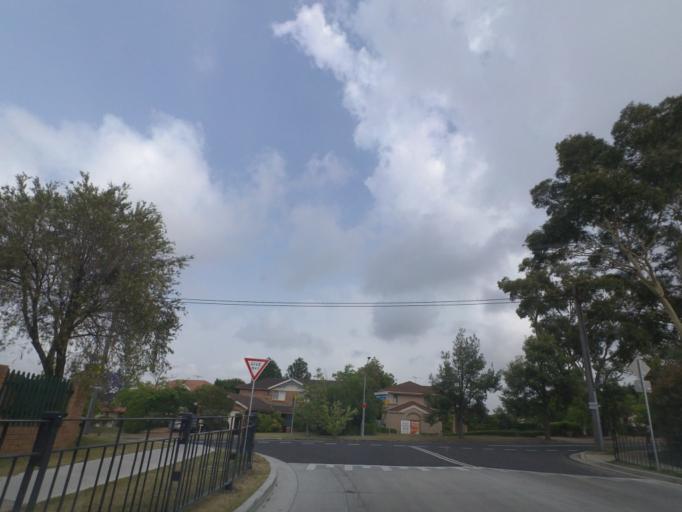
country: AU
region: New South Wales
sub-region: The Hills Shire
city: West Pennant
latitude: -33.7338
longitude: 151.0375
